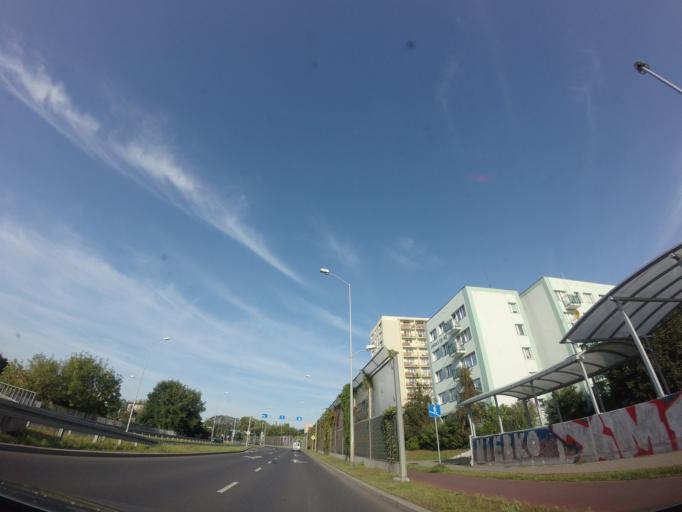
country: PL
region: West Pomeranian Voivodeship
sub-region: Szczecin
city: Szczecin
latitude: 53.4550
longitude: 14.5398
